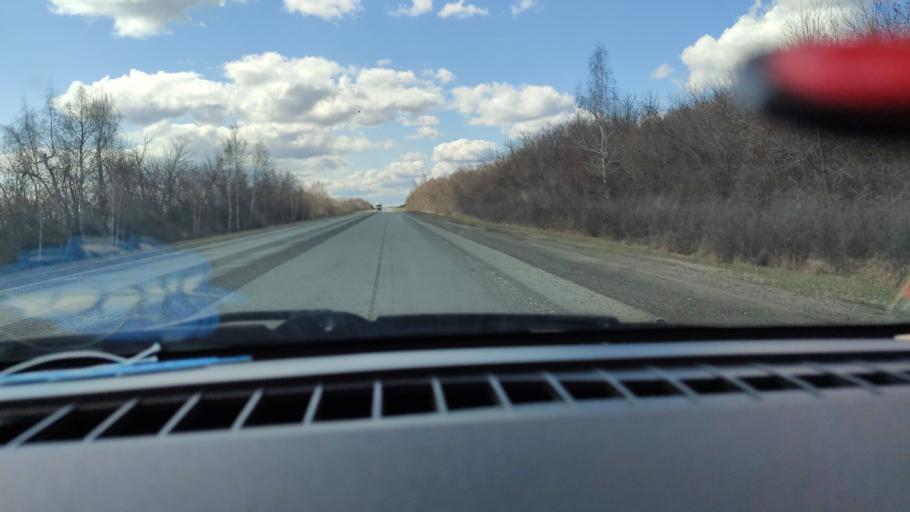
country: RU
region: Saratov
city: Dukhovnitskoye
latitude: 52.6367
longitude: 48.1885
